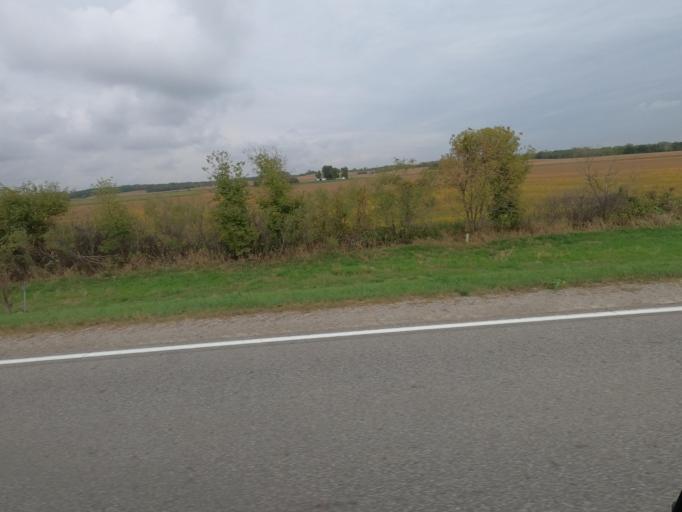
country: US
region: Iowa
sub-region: Wapello County
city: Ottumwa
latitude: 40.9000
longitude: -92.1926
